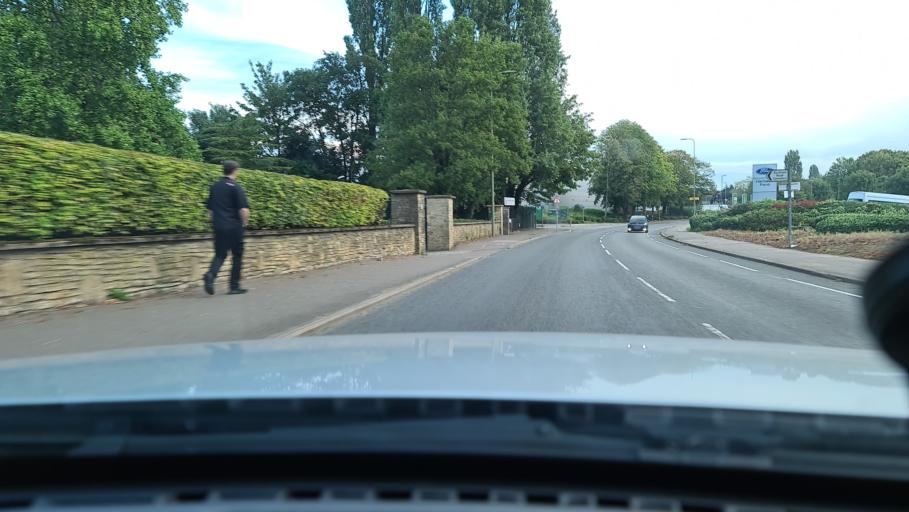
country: GB
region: England
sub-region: Oxfordshire
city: Banbury
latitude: 52.0677
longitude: -1.3405
